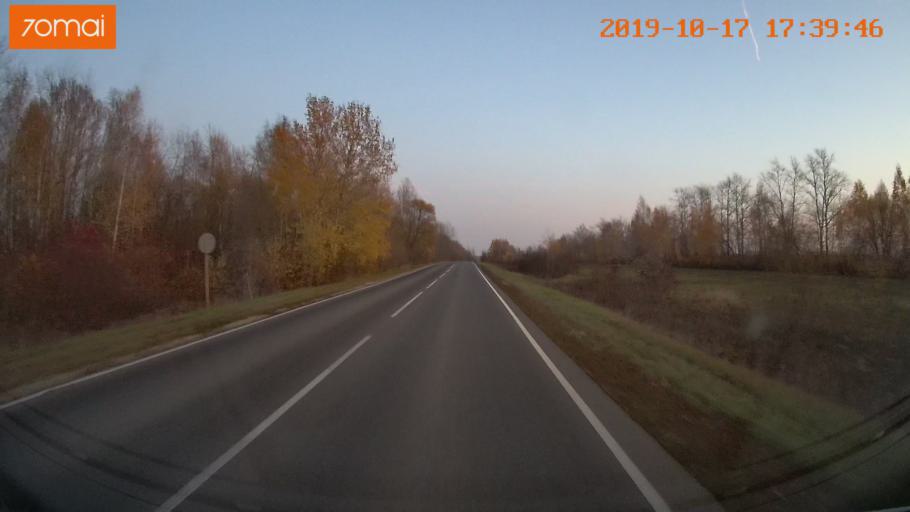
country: RU
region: Tula
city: Yepifan'
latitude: 53.8004
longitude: 38.5970
